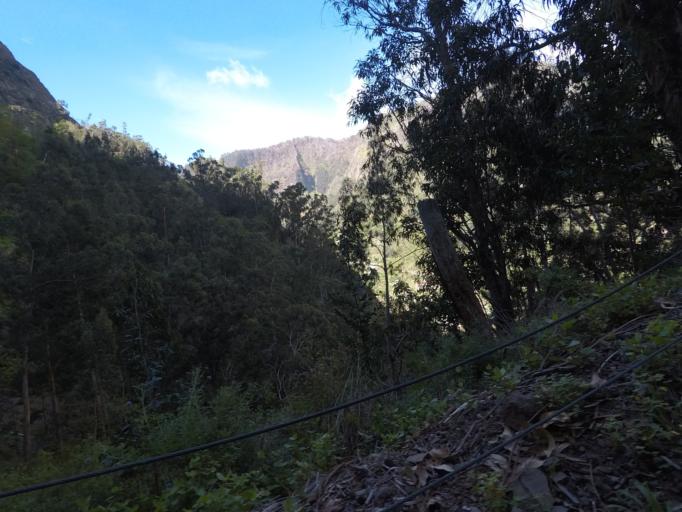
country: PT
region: Madeira
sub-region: Camara de Lobos
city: Curral das Freiras
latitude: 32.7152
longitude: -16.9643
